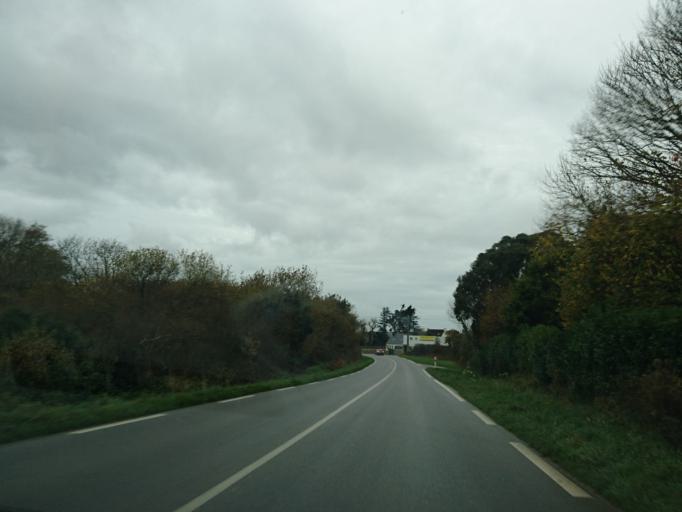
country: FR
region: Brittany
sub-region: Departement du Finistere
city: Plouzane
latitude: 48.3636
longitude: -4.6613
